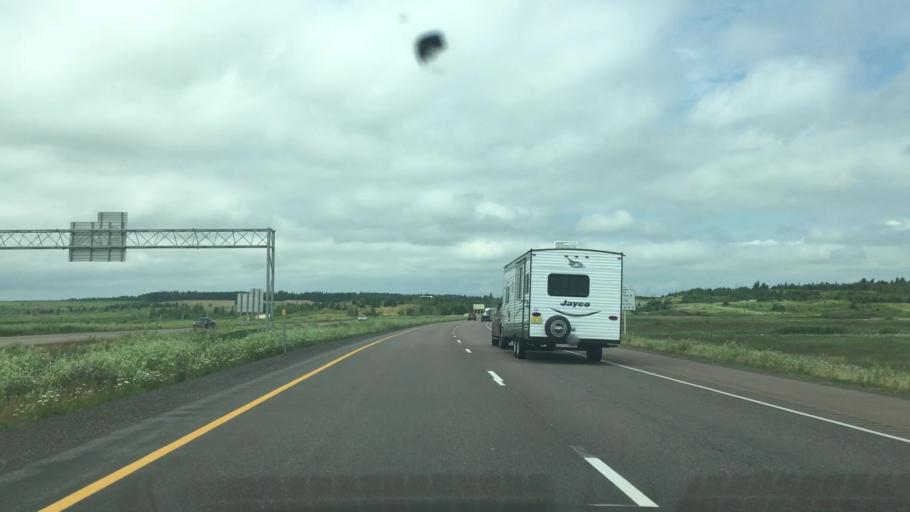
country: CA
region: Nova Scotia
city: Amherst
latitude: 45.8595
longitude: -64.2688
